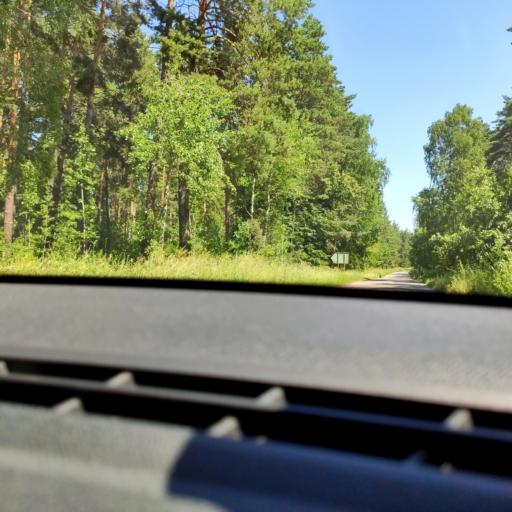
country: RU
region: Samara
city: Podstepki
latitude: 53.5678
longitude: 49.0242
